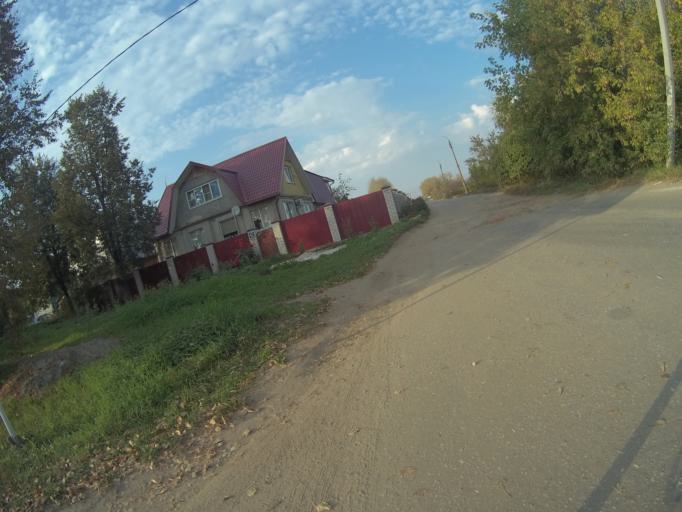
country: RU
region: Vladimir
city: Bogolyubovo
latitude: 56.1914
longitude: 40.4938
